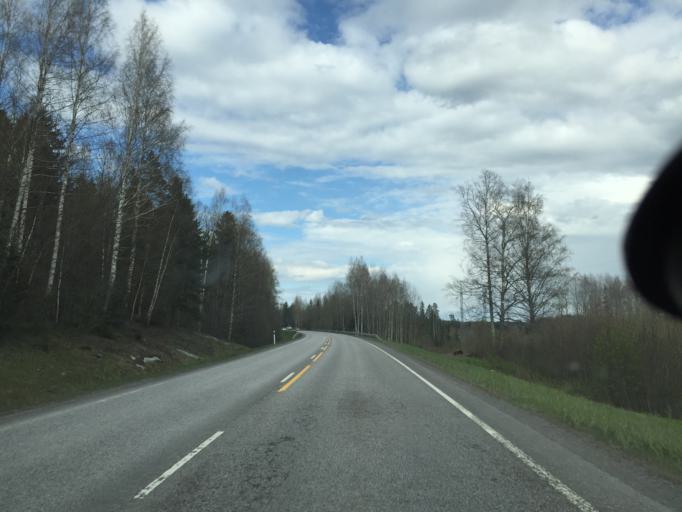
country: FI
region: Uusimaa
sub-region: Helsinki
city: Lohja
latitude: 60.1820
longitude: 24.0048
